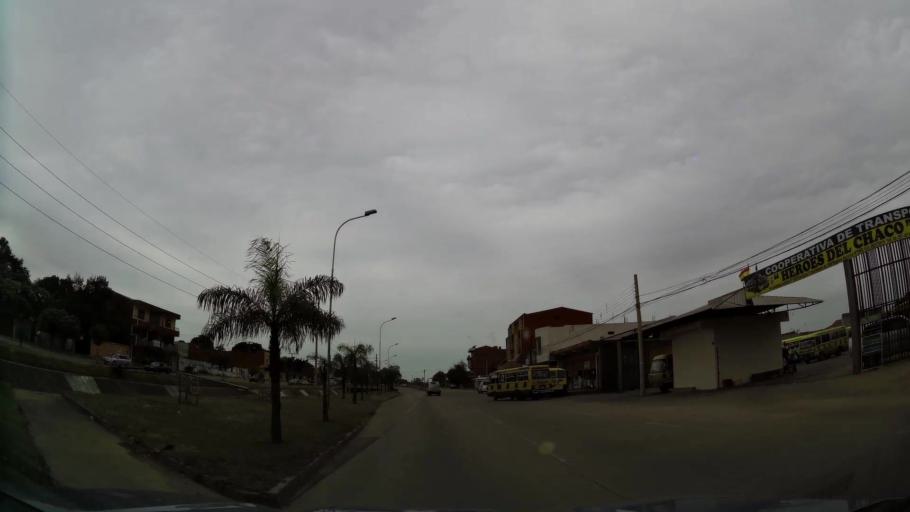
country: BO
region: Santa Cruz
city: Santa Cruz de la Sierra
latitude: -17.8191
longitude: -63.1706
